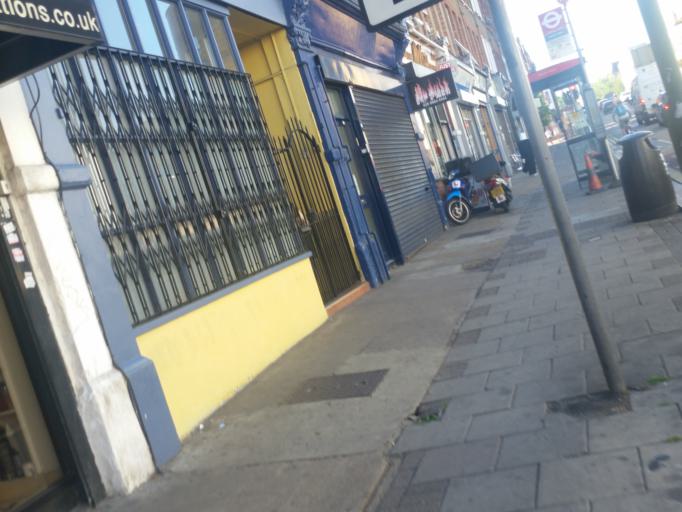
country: GB
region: England
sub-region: Greater London
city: Bayswater
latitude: 51.5305
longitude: -0.2164
